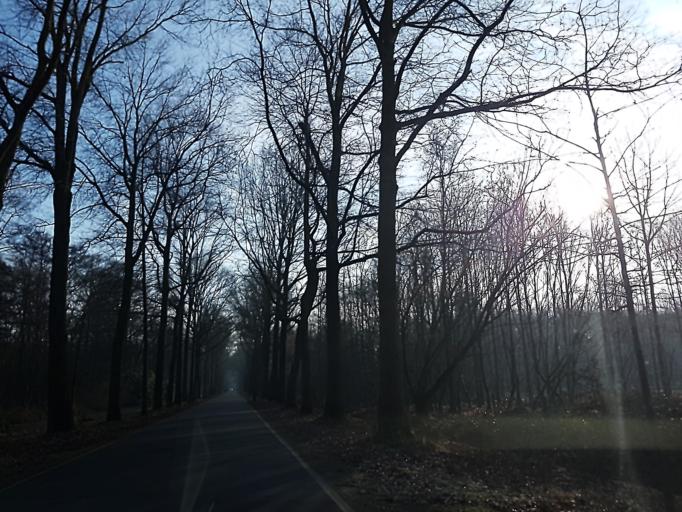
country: BE
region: Flanders
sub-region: Provincie Antwerpen
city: Brasschaat
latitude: 51.3137
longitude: 4.5313
